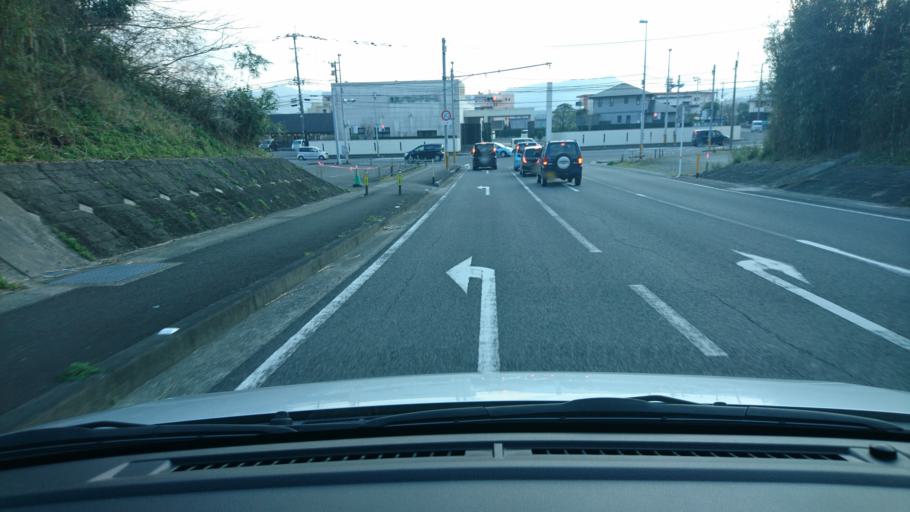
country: JP
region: Miyazaki
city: Miyazaki-shi
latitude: 31.8555
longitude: 131.3987
